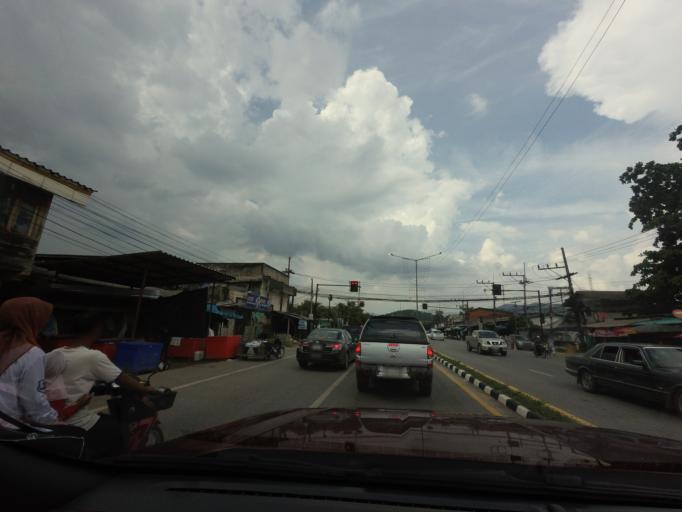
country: TH
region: Yala
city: Ban Nang Sata
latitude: 6.2658
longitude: 101.2624
